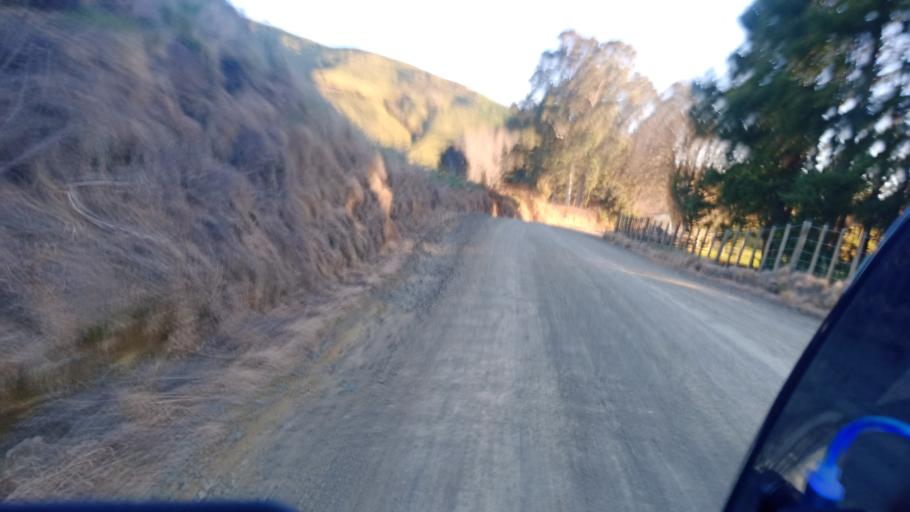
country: NZ
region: Bay of Plenty
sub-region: Opotiki District
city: Opotiki
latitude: -38.4599
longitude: 177.4255
